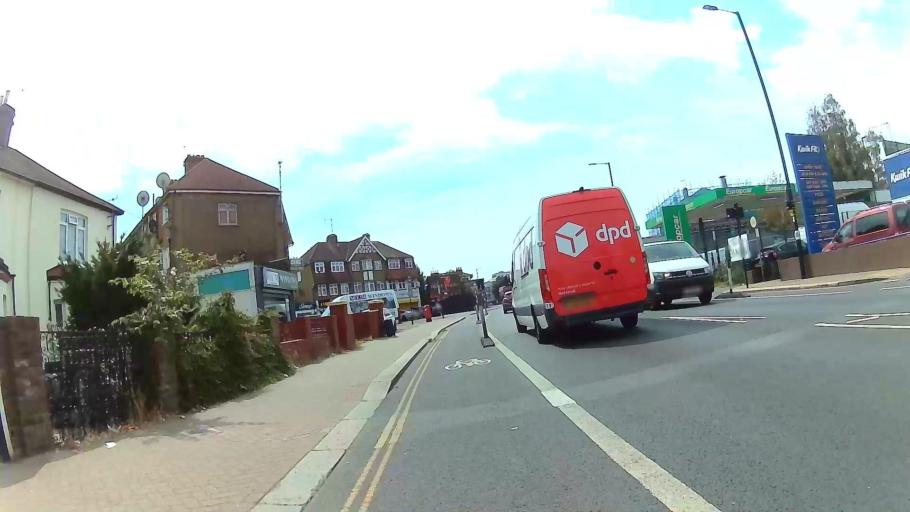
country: GB
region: England
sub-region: Hertfordshire
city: Waltham Cross
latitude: 51.6646
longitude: -0.0441
